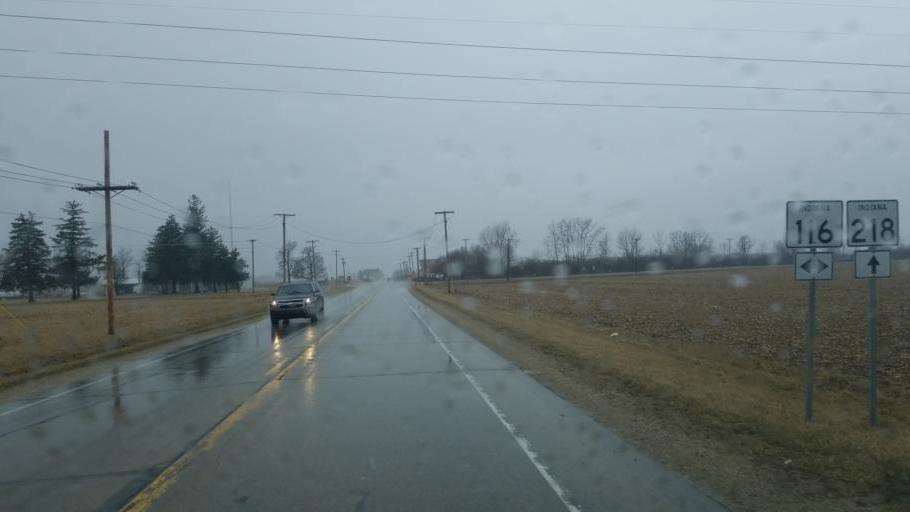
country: US
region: Indiana
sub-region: Adams County
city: Berne
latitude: 40.6557
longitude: -85.0449
